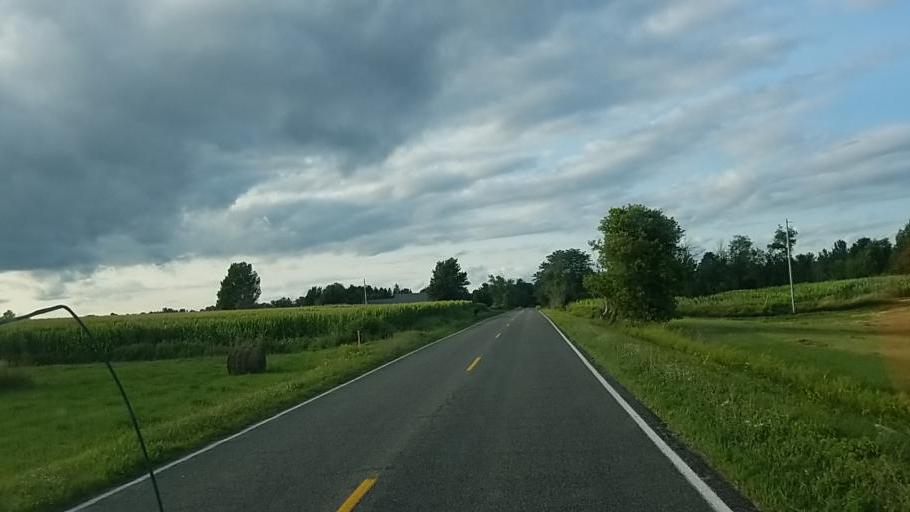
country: US
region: Michigan
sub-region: Montcalm County
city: Howard City
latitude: 43.3010
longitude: -85.3635
